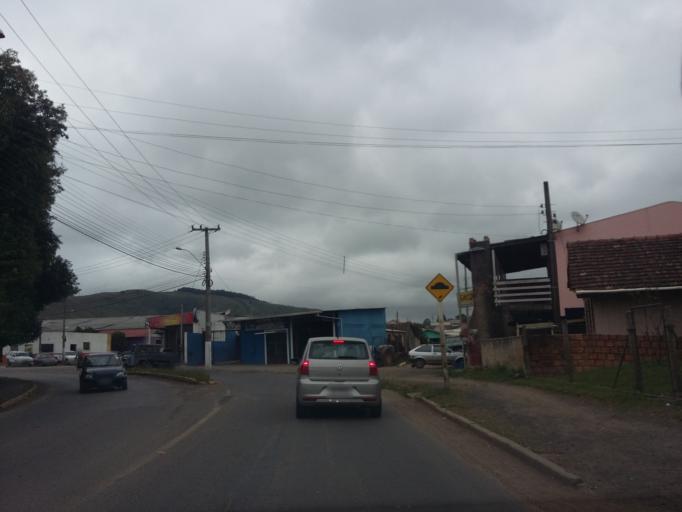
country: BR
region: Santa Catarina
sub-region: Lages
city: Lages
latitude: -27.8105
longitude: -50.2931
